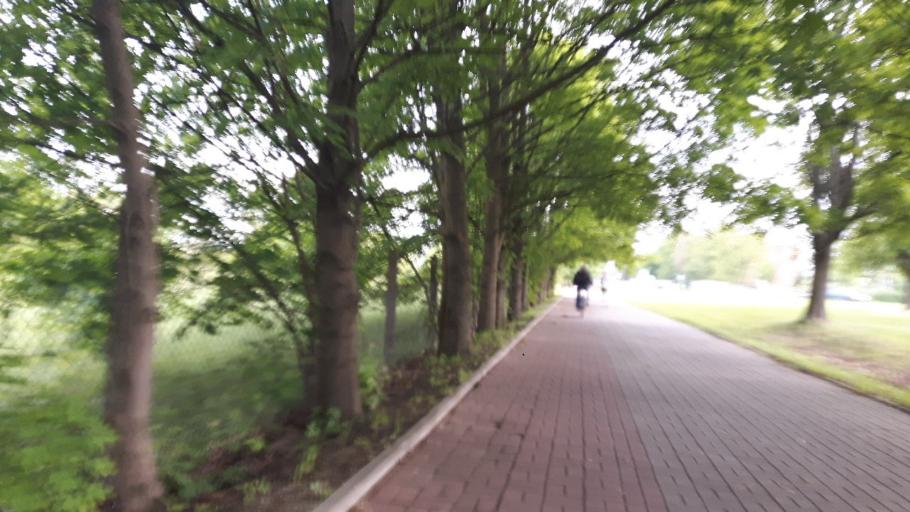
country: PL
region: West Pomeranian Voivodeship
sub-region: Powiat policki
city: Przeclaw
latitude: 53.3937
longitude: 14.4890
